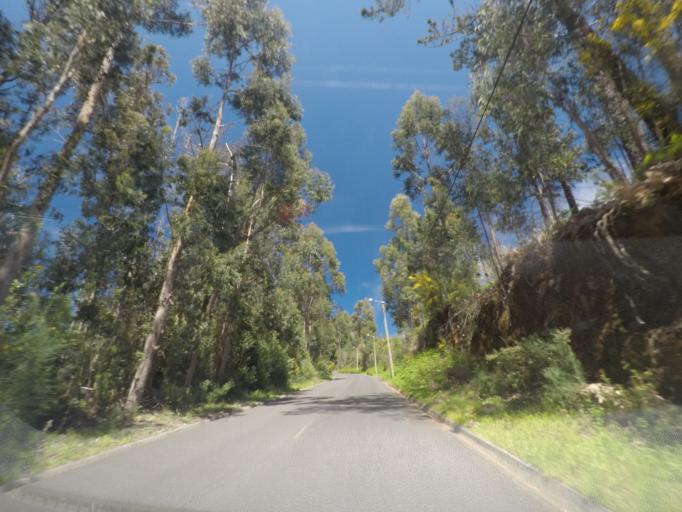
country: PT
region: Madeira
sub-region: Calheta
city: Arco da Calheta
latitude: 32.7311
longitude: -17.1326
